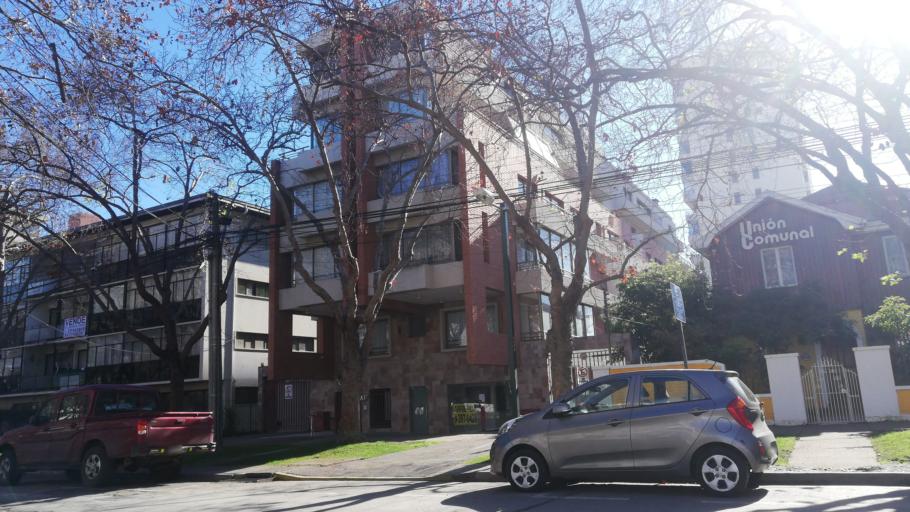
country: CL
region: Valparaiso
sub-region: Provincia de Valparaiso
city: Vina del Mar
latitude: -33.0156
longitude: -71.5480
